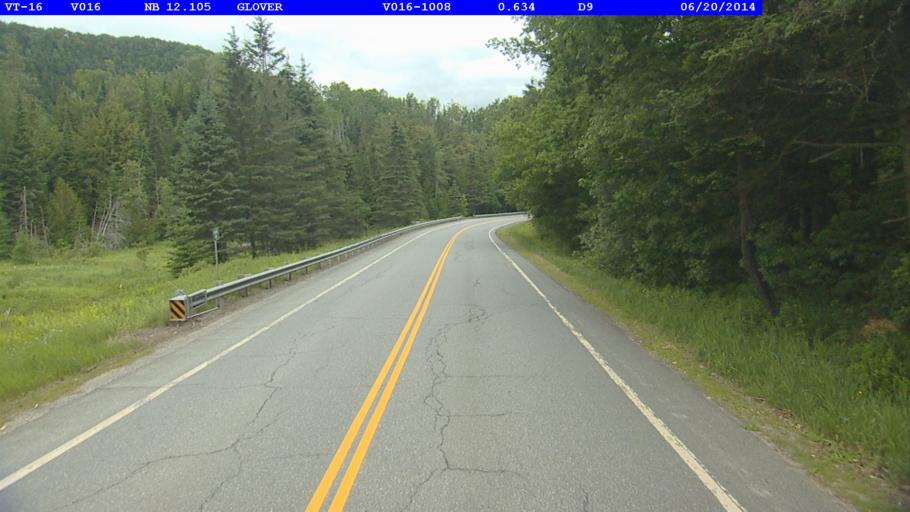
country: US
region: Vermont
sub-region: Caledonia County
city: Hardwick
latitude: 44.6369
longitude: -72.2108
